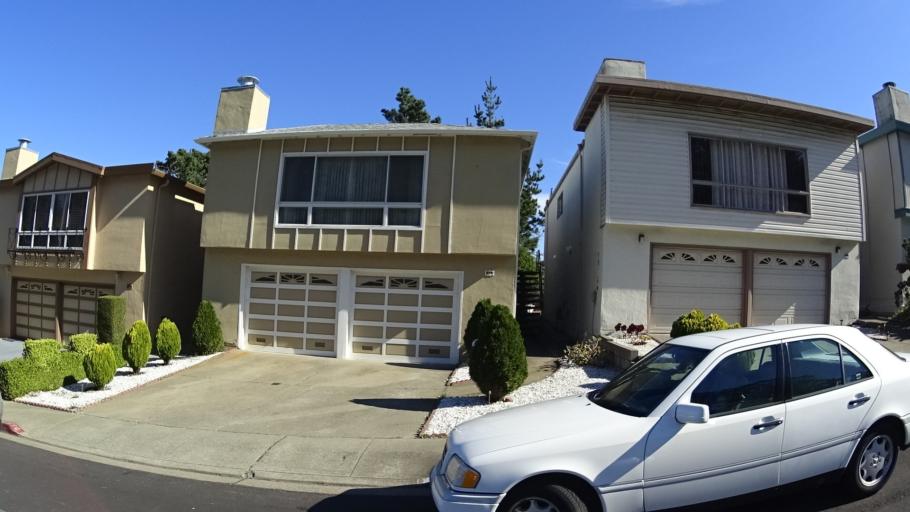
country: US
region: California
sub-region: San Mateo County
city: Colma
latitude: 37.6548
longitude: -122.4712
